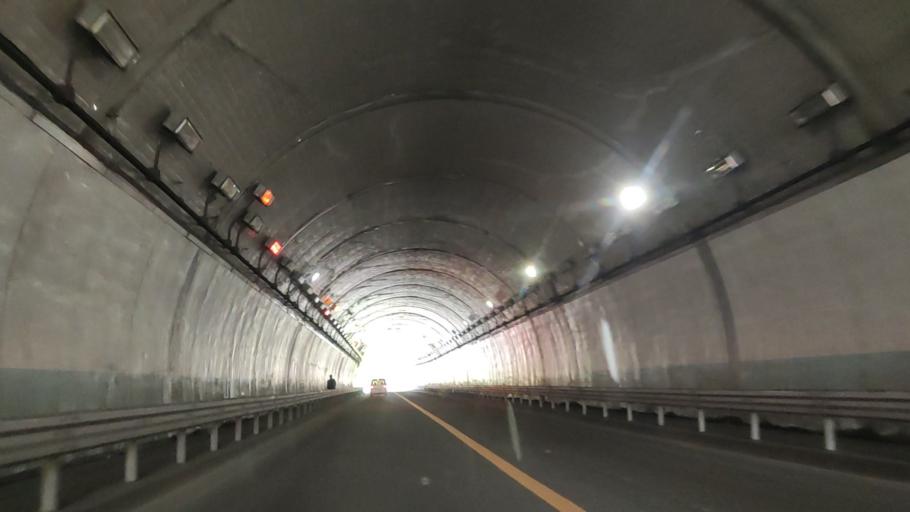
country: JP
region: Kanagawa
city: Yokohama
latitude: 35.3997
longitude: 139.6088
